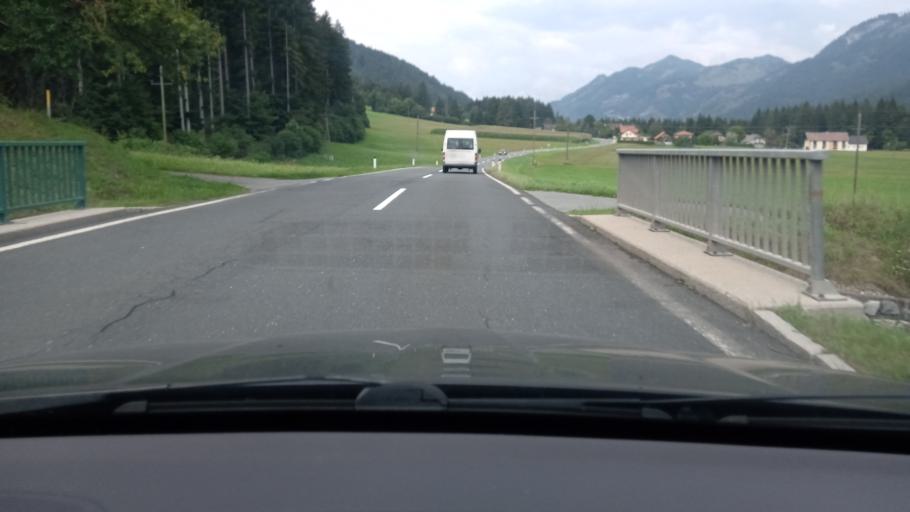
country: AT
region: Carinthia
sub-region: Politischer Bezirk Hermagor
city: Hermagor
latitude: 46.6422
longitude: 13.3404
